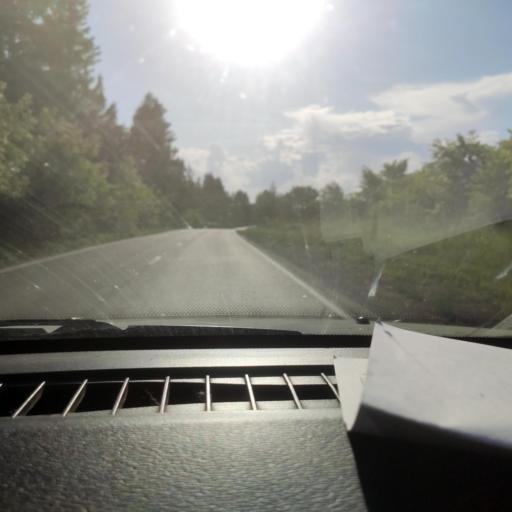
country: RU
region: Perm
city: Krasnokamsk
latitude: 58.1328
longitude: 55.7691
